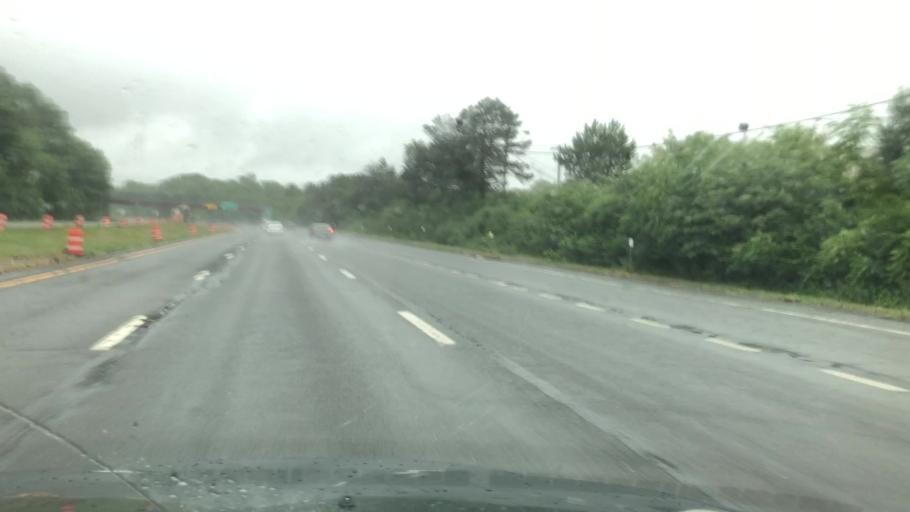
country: US
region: New York
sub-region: Orange County
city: Balmville
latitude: 41.5197
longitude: -74.0274
